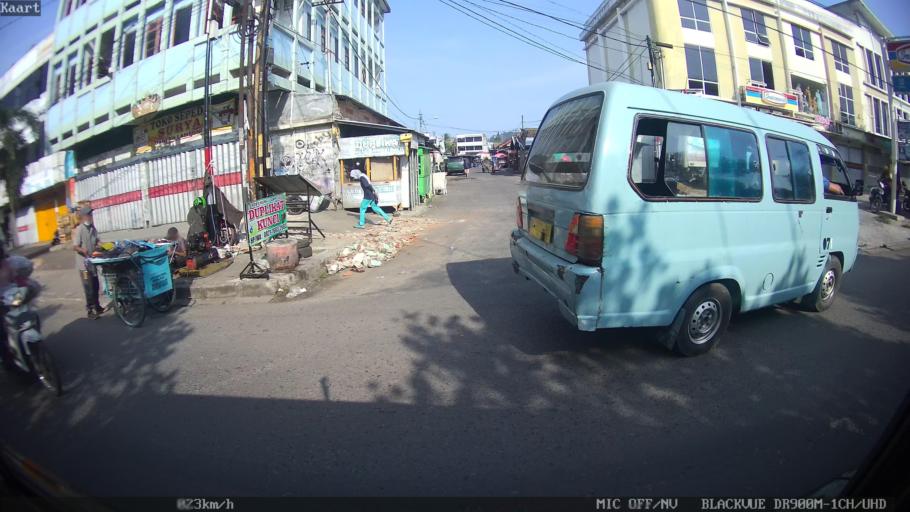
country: ID
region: Lampung
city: Bandarlampung
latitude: -5.4080
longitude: 105.2570
